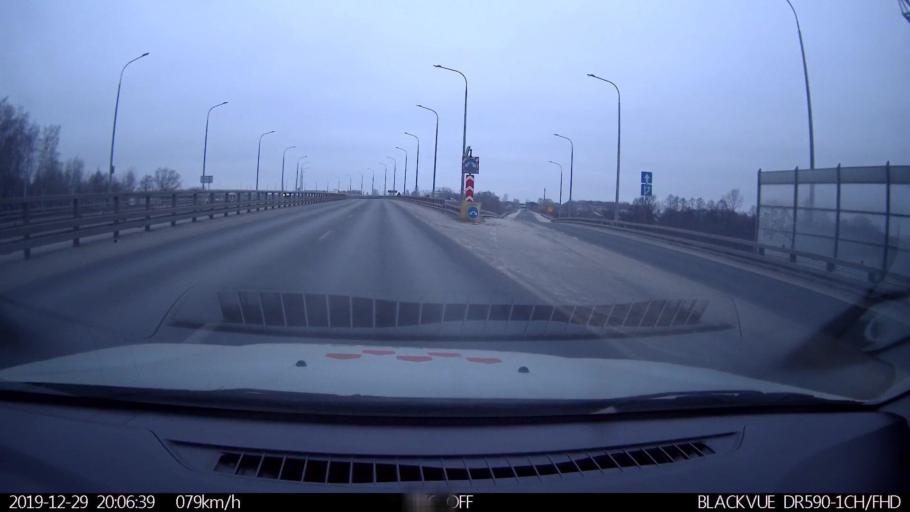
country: RU
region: Nizjnij Novgorod
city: Neklyudovo
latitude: 56.3965
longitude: 43.9978
